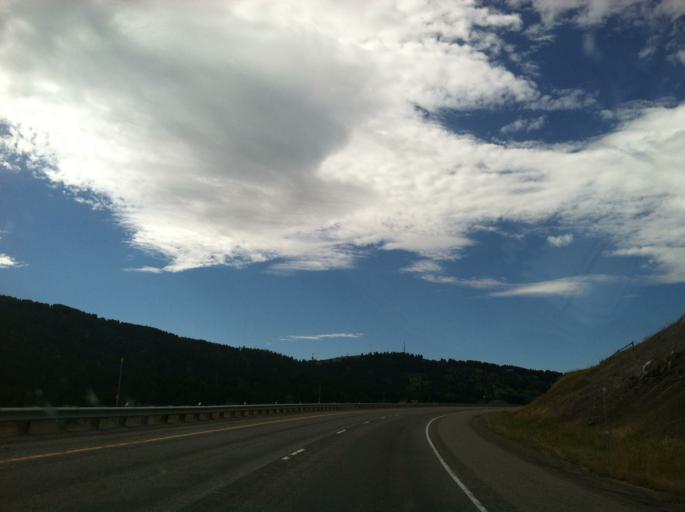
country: US
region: Montana
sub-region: Park County
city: Livingston
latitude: 45.6564
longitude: -110.7760
